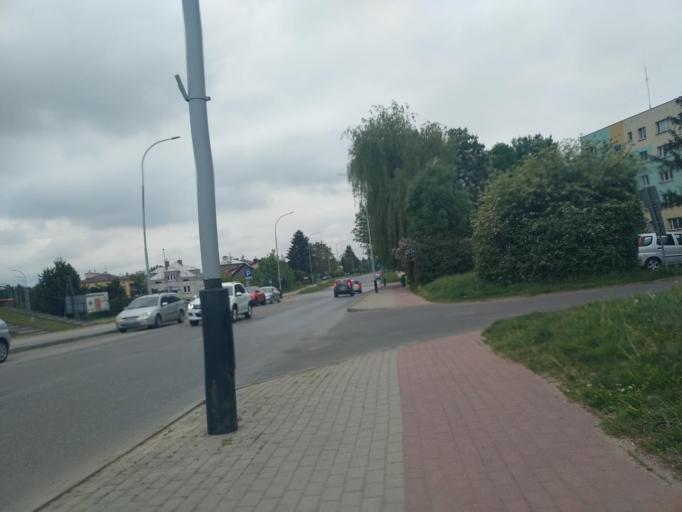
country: PL
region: Subcarpathian Voivodeship
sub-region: Krosno
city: Krosno
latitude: 49.6826
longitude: 21.7593
